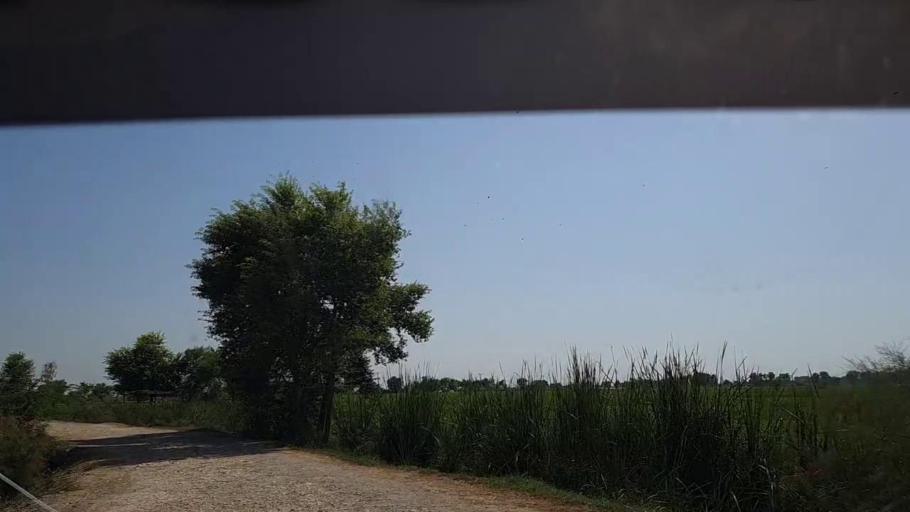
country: PK
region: Sindh
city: Ghauspur
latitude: 28.2166
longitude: 69.0904
